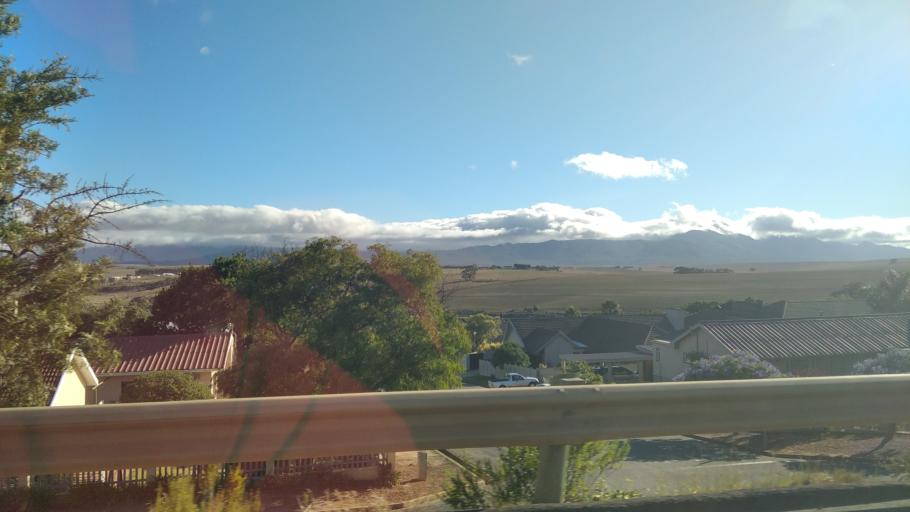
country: ZA
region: Western Cape
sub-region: Overberg District Municipality
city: Caledon
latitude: -34.2267
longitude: 19.4207
